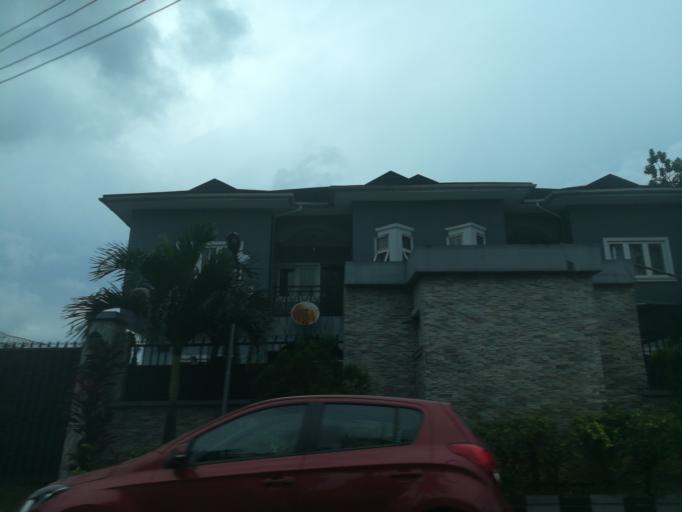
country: NG
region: Rivers
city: Port Harcourt
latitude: 4.8207
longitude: 6.9998
